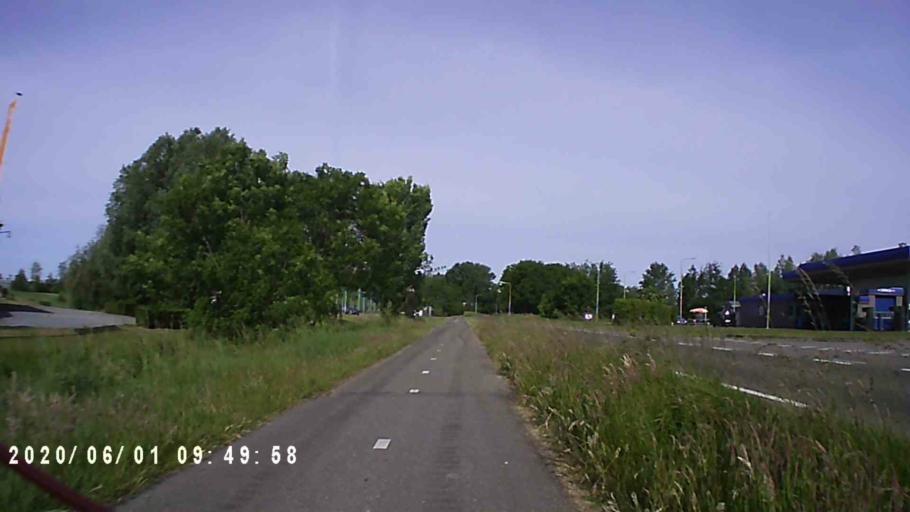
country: NL
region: Friesland
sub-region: Menameradiel
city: Berltsum
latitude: 53.2413
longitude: 5.6648
